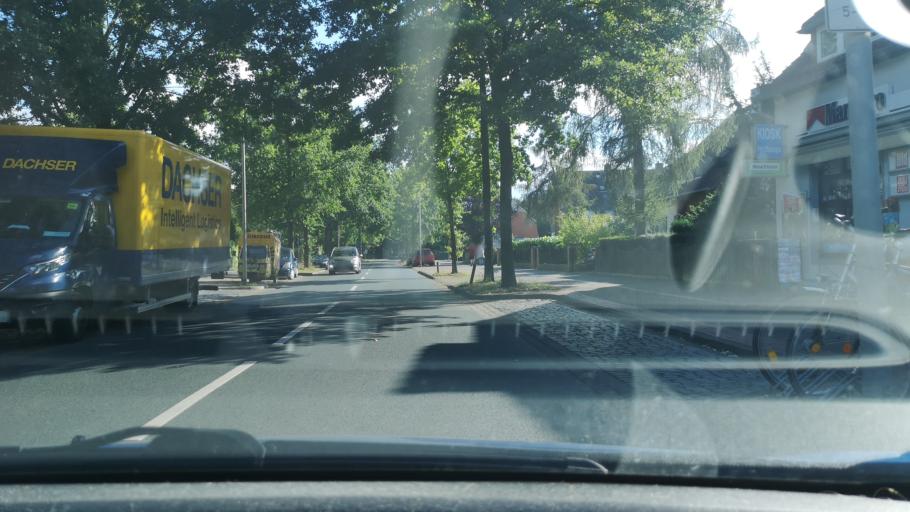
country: DE
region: Lower Saxony
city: Isernhagen Farster Bauerschaft
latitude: 52.4121
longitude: 9.8052
